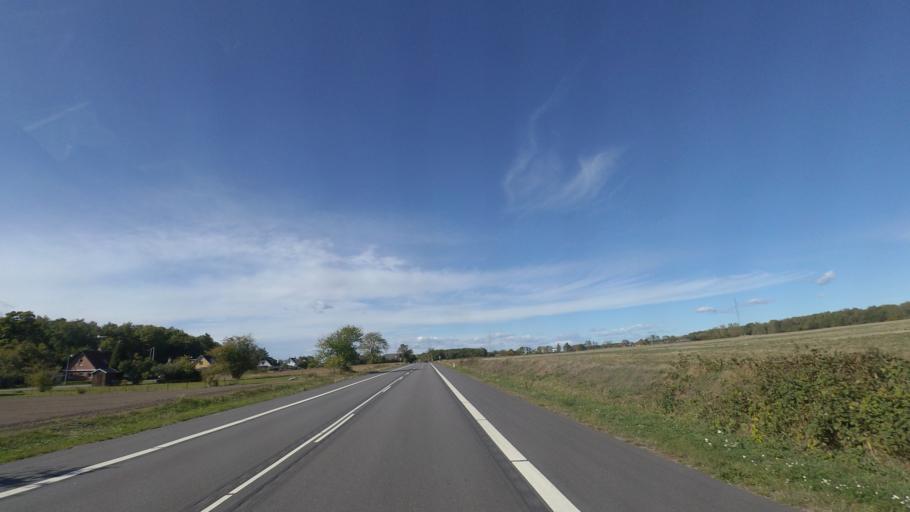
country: DK
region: Capital Region
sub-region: Bornholm Kommune
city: Ronne
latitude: 55.0875
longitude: 14.7430
